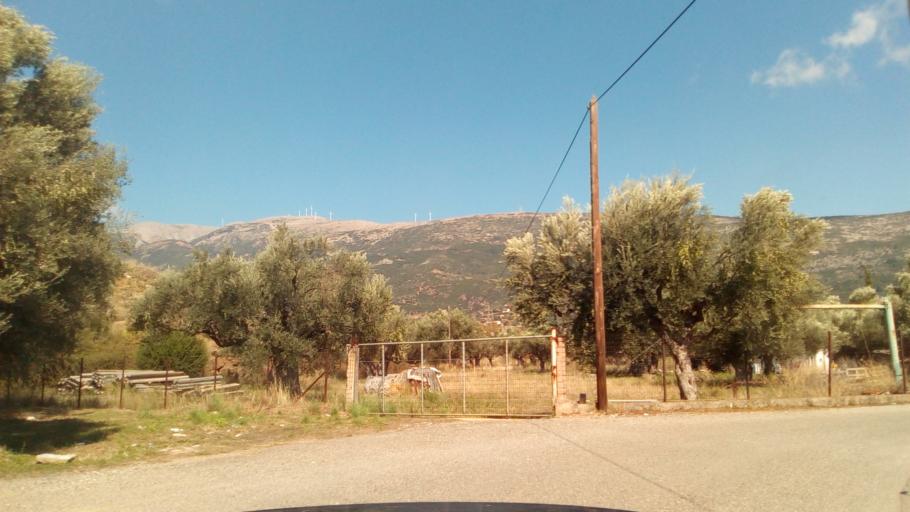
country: GR
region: West Greece
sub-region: Nomos Aitolias kai Akarnanias
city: Nafpaktos
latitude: 38.3904
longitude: 21.7974
